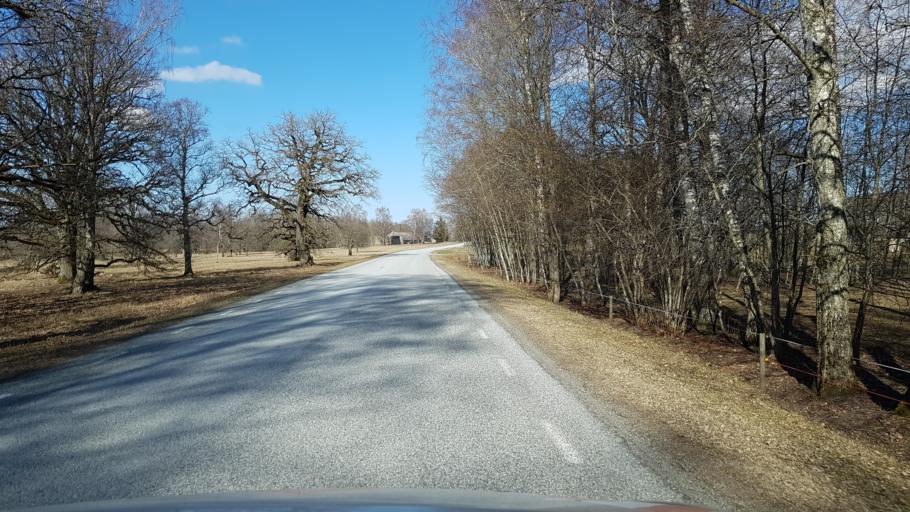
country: EE
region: Laeaene-Virumaa
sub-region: Rakvere linn
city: Rakvere
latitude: 59.3223
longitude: 26.2680
